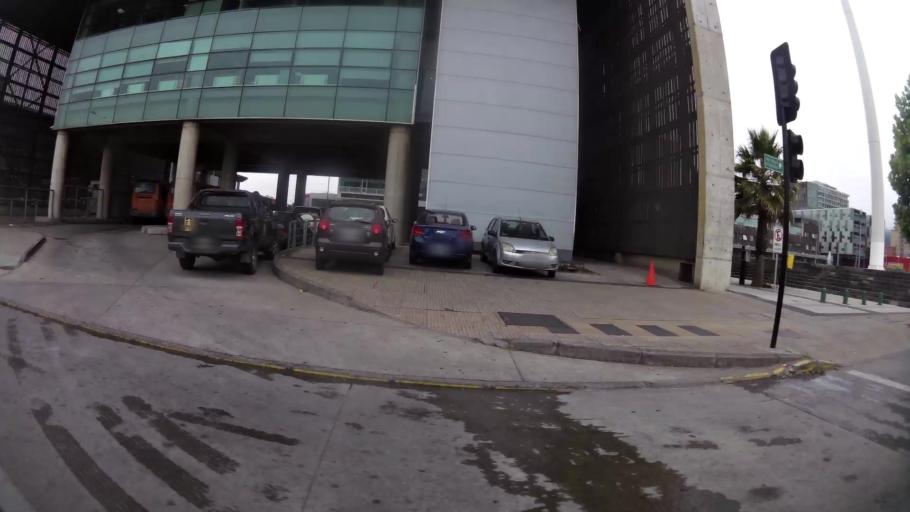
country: CL
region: Biobio
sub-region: Provincia de Concepcion
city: Concepcion
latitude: -36.8300
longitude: -73.0608
